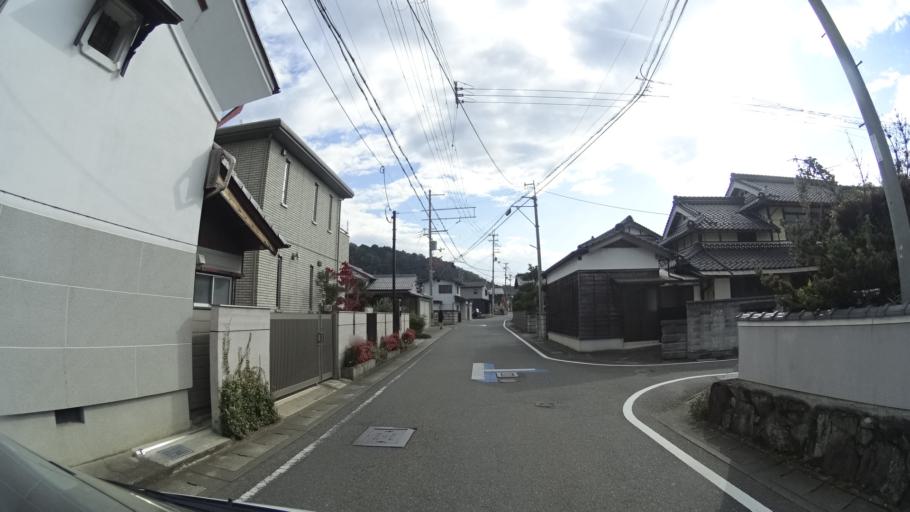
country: JP
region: Kyoto
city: Fukuchiyama
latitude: 35.3014
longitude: 135.1783
